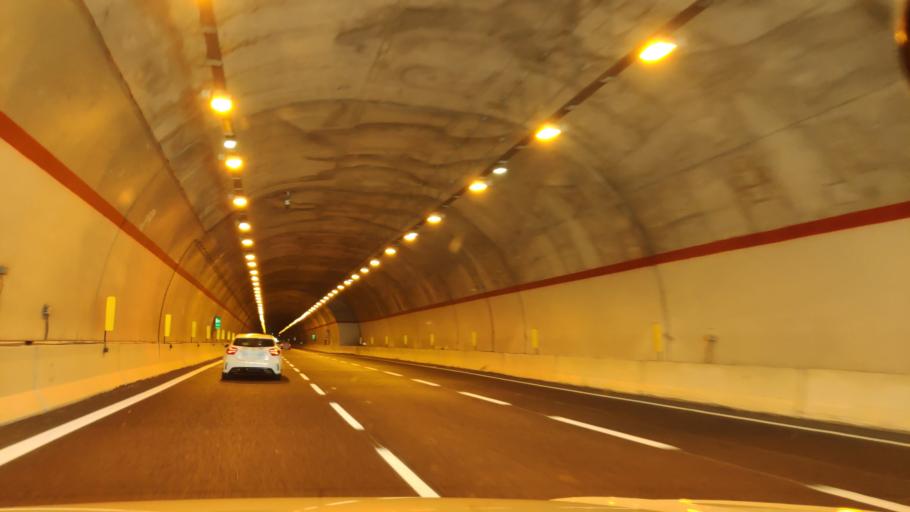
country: IT
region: Calabria
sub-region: Provincia di Cosenza
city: Mormanno
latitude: 39.9007
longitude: 15.9736
